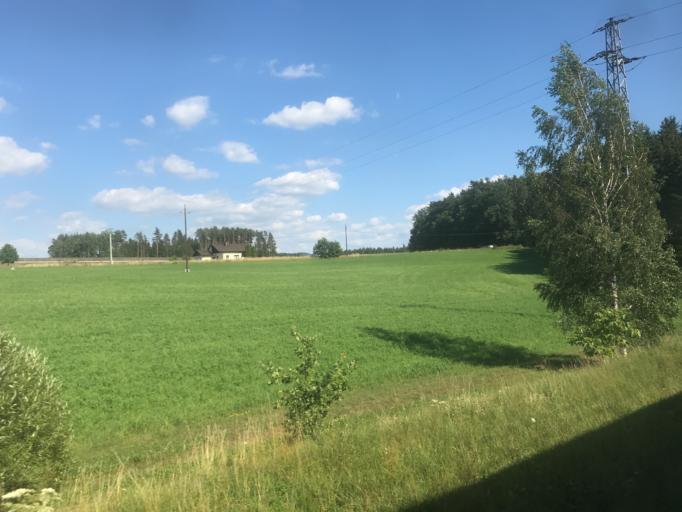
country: AT
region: Upper Austria
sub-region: Politischer Bezirk Freistadt
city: Freistadt
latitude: 48.4688
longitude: 14.4983
